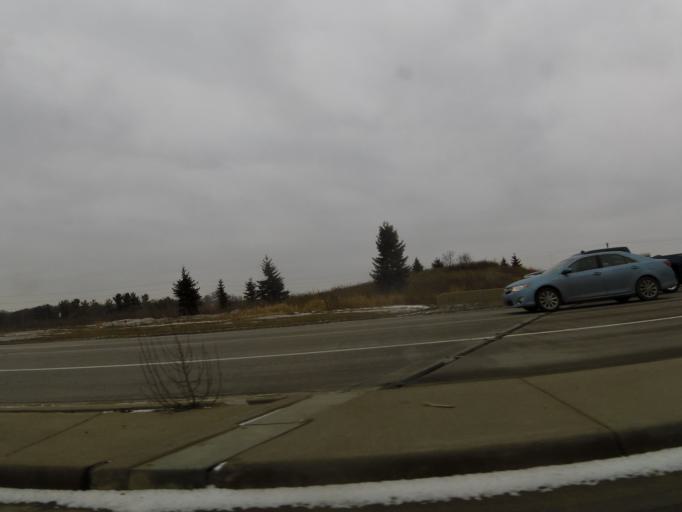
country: US
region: Minnesota
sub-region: Carver County
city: Chaska
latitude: 44.8059
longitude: -93.6248
